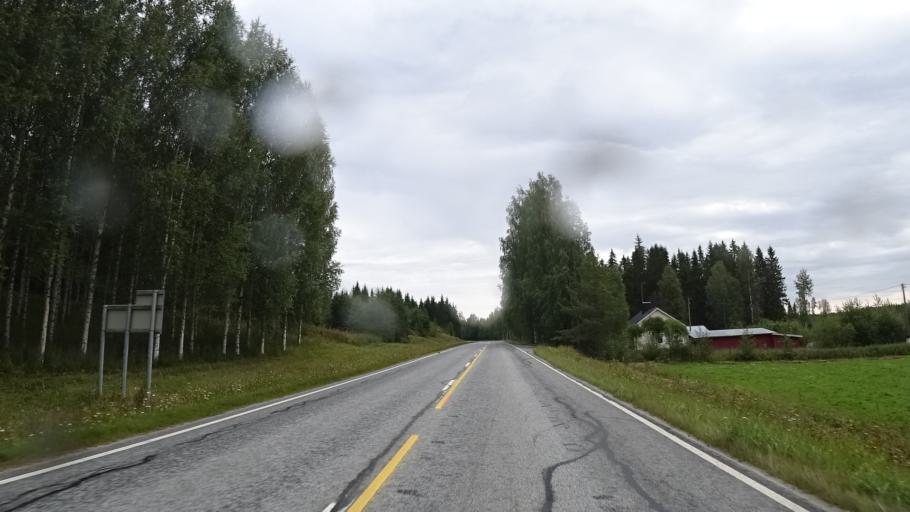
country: FI
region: North Karelia
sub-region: Keski-Karjala
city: Kesaelahti
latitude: 62.1102
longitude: 29.7455
